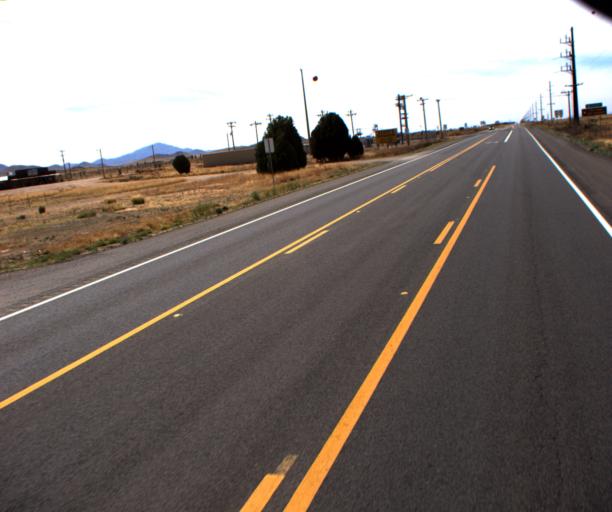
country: US
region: Arizona
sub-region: Cochise County
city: Willcox
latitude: 31.8853
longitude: -109.6952
